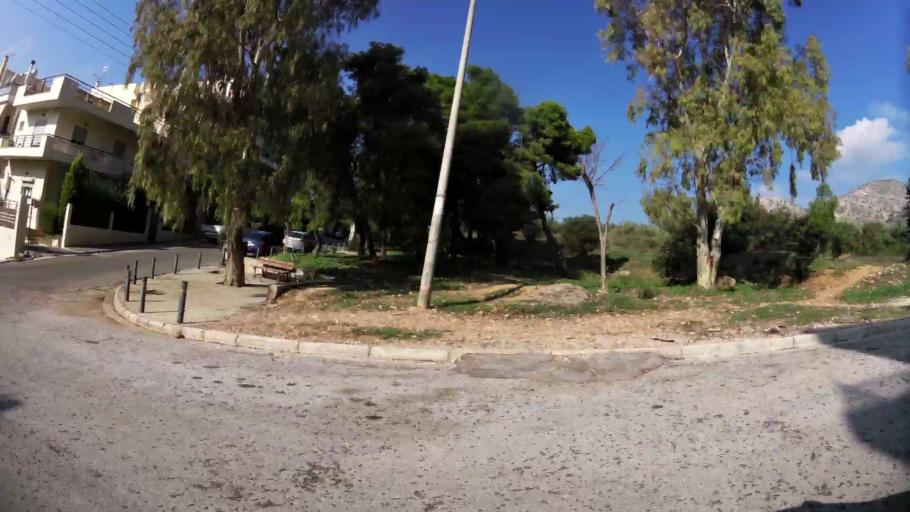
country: GR
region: Attica
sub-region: Nomarchia Athinas
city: Argyroupoli
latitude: 37.9113
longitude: 23.7579
